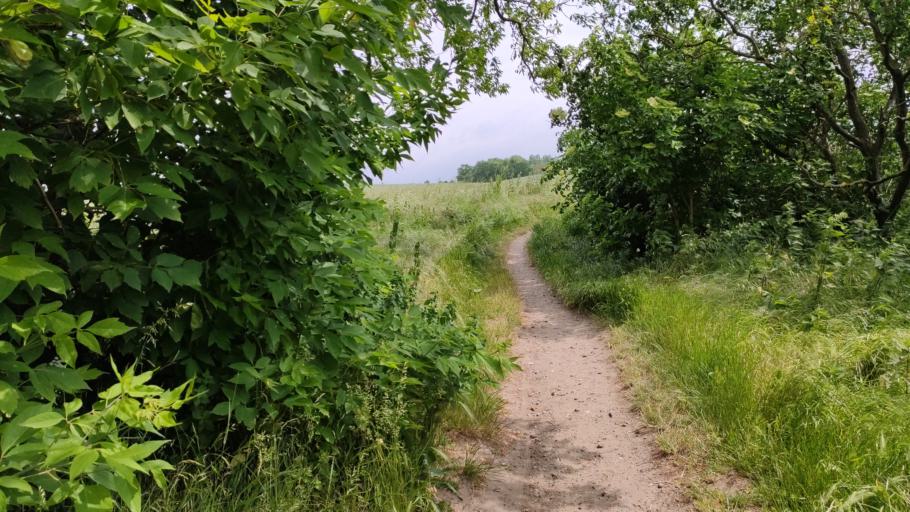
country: DE
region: Mecklenburg-Vorpommern
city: Bastorf
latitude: 54.1158
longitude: 11.6249
